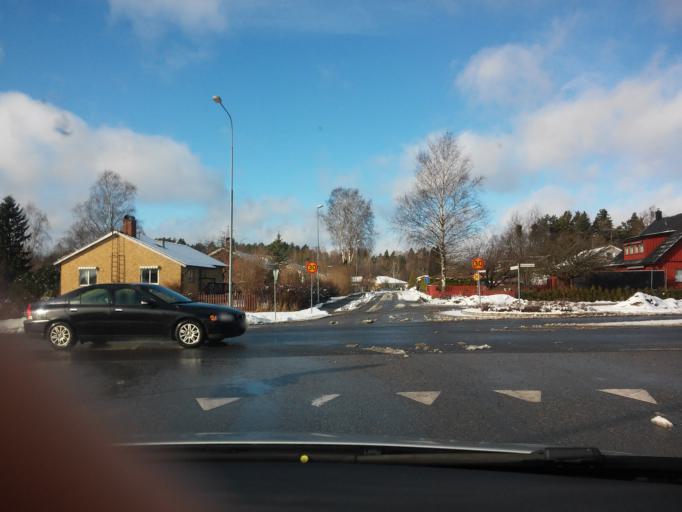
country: SE
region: Stockholm
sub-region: Osterakers Kommun
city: Akersberga
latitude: 59.4944
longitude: 18.2792
